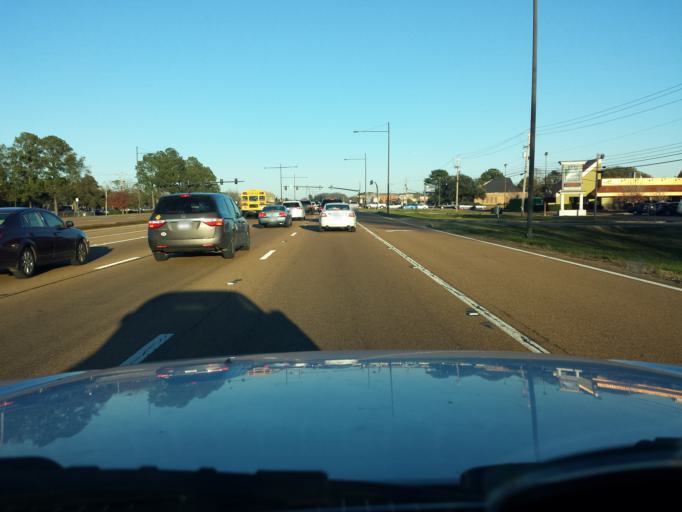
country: US
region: Mississippi
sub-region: Rankin County
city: Flowood
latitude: 32.3306
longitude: -90.1101
